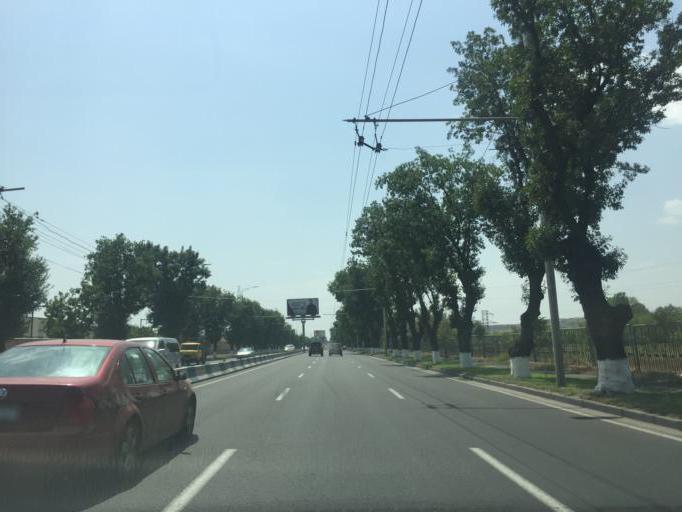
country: AM
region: Yerevan
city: Yerevan
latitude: 40.1655
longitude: 44.4807
